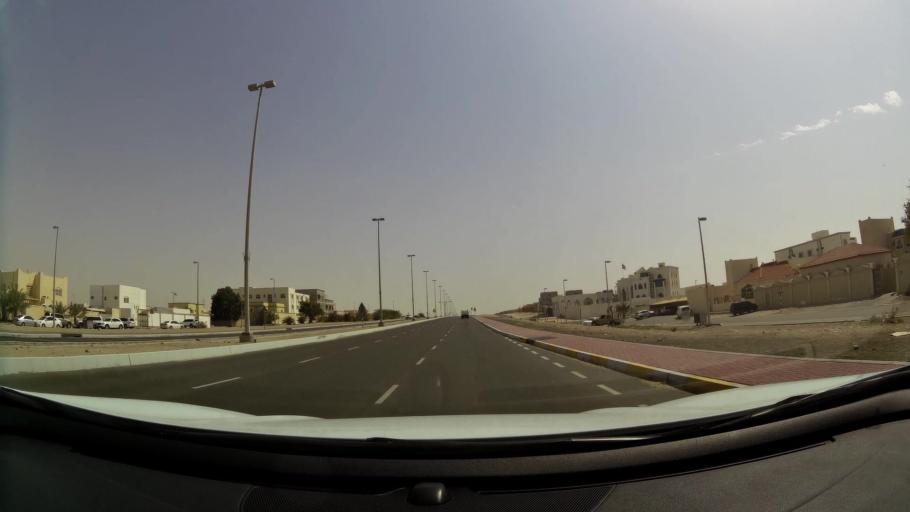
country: AE
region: Abu Dhabi
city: Abu Dhabi
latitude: 24.2978
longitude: 54.6509
